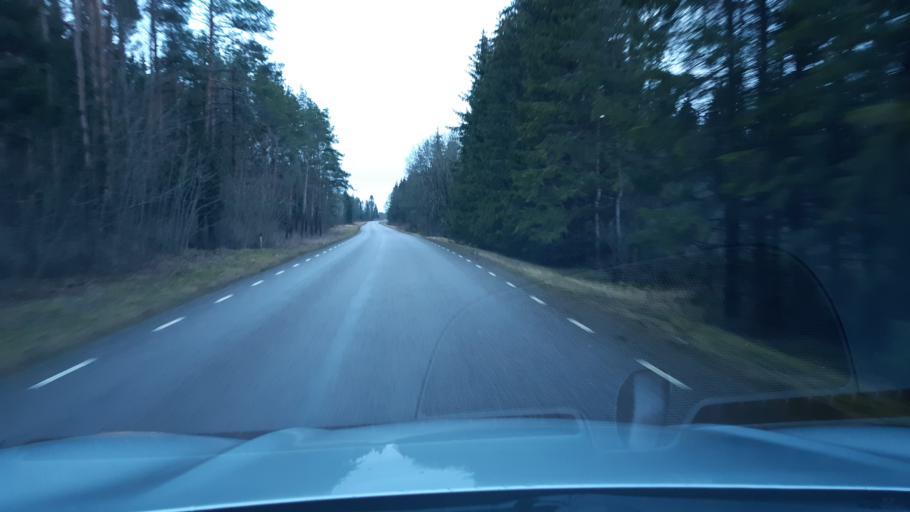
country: EE
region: Raplamaa
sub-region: Kohila vald
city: Kohila
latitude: 59.1266
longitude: 24.6709
